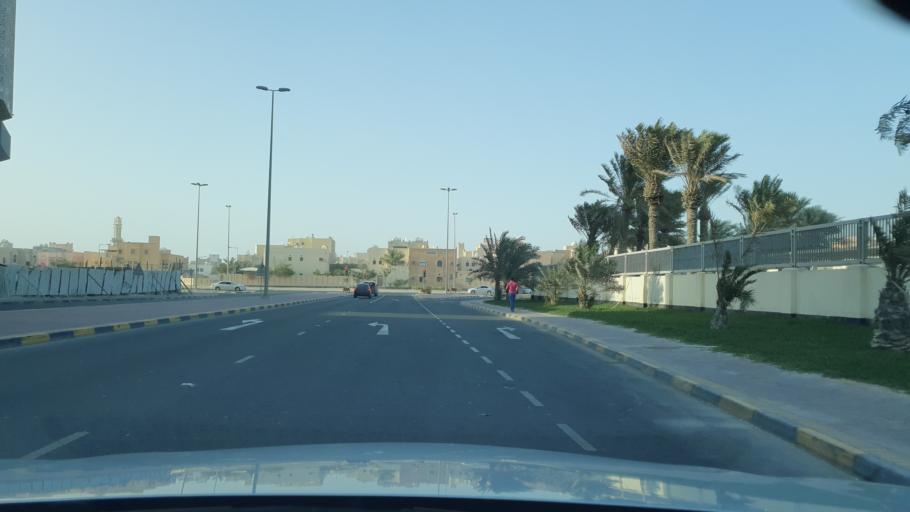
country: BH
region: Muharraq
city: Al Muharraq
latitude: 26.2656
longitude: 50.5980
